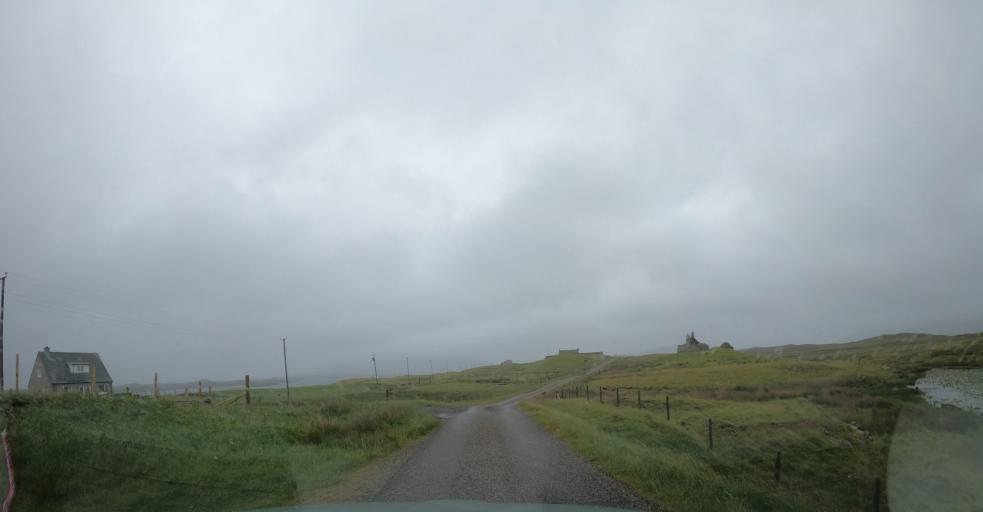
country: GB
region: Scotland
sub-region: Eilean Siar
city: Isle of North Uist
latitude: 57.5505
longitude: -7.2235
